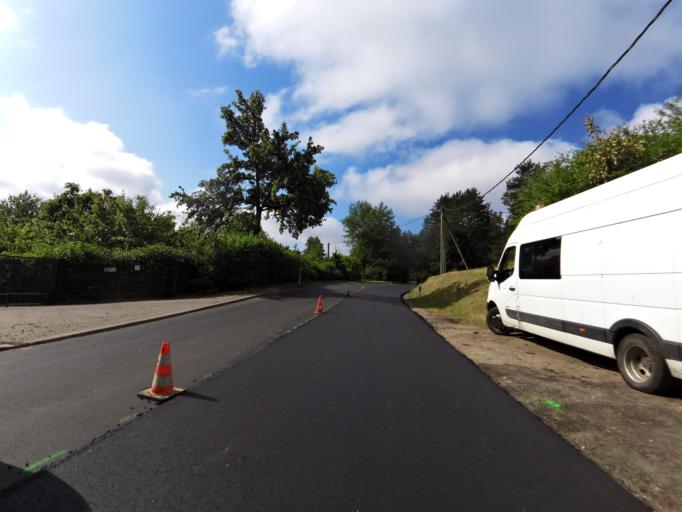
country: LT
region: Vilnius County
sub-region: Vilnius
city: Fabijoniskes
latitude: 54.7416
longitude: 25.2902
